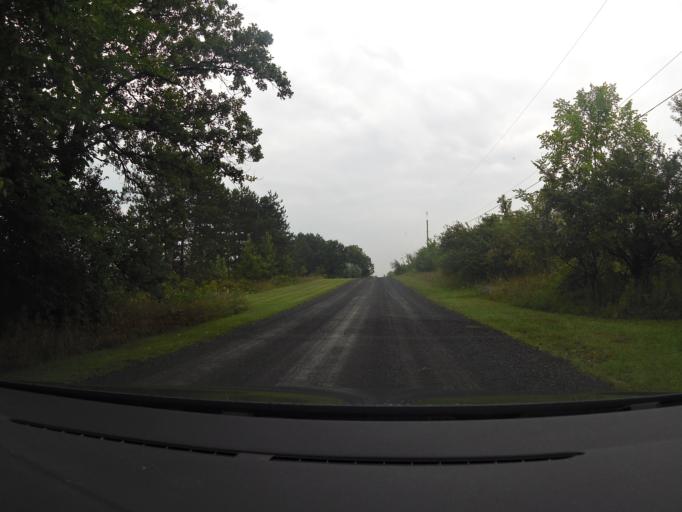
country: CA
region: Ontario
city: Carleton Place
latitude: 45.1872
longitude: -76.0645
